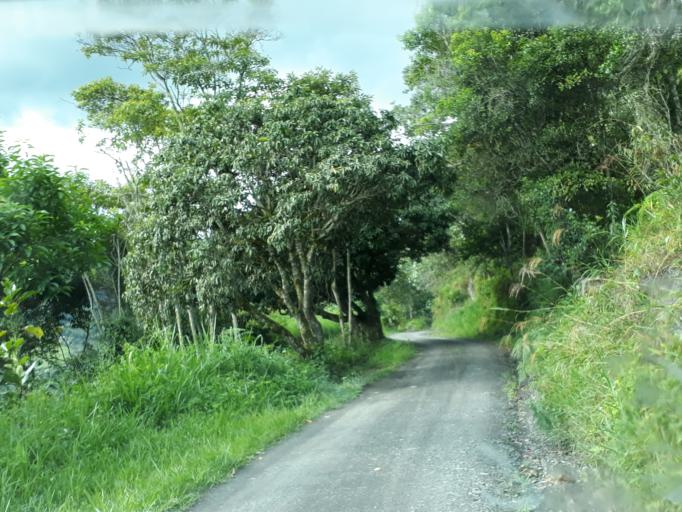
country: CO
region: Cundinamarca
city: Pacho
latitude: 5.1831
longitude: -74.2527
